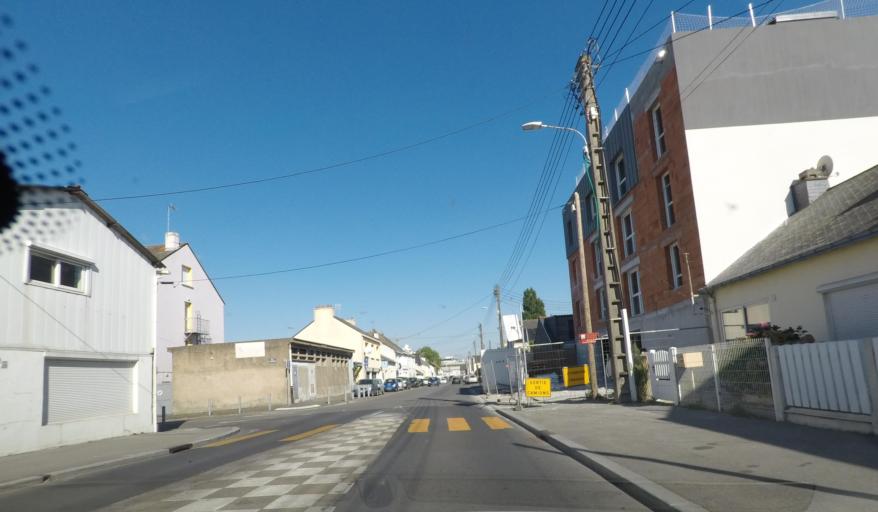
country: FR
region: Pays de la Loire
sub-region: Departement de la Loire-Atlantique
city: Saint-Nazaire
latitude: 47.2851
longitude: -2.2076
